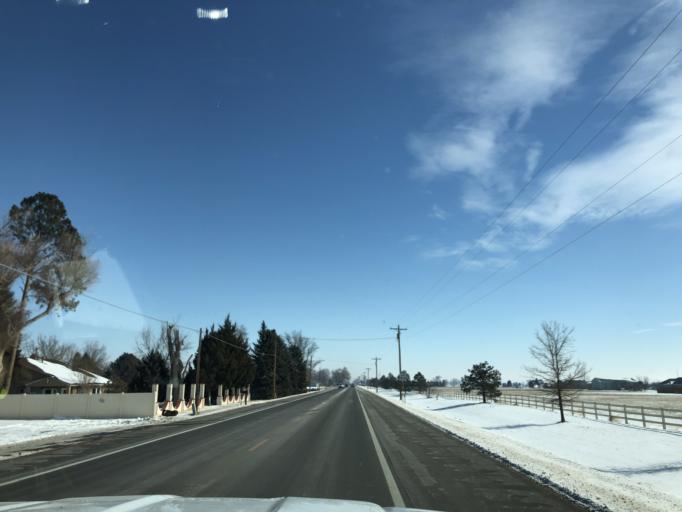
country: US
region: Colorado
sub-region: Morgan County
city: Fort Morgan
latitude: 40.2540
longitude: -103.8475
